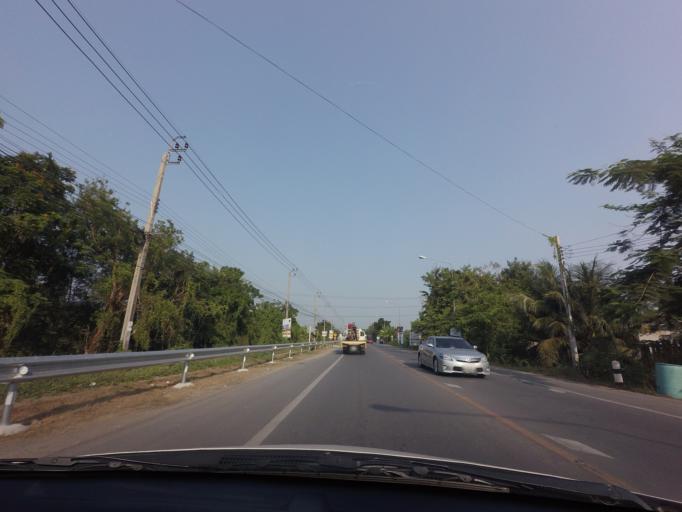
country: TH
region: Bangkok
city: Thawi Watthana
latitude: 13.8100
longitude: 100.3545
